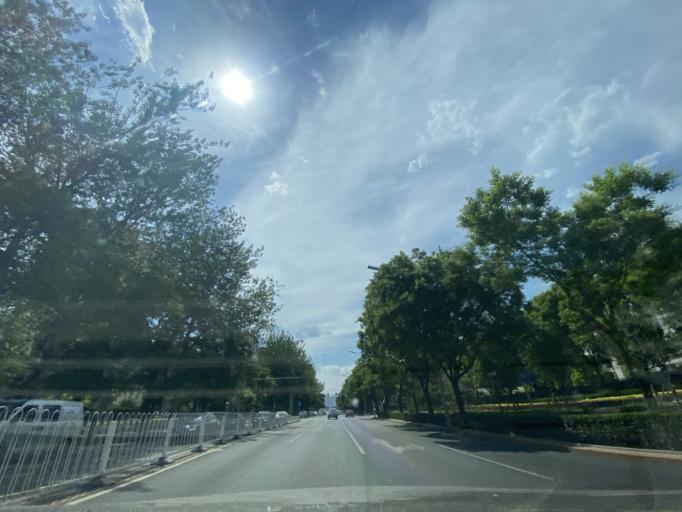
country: CN
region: Beijing
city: Lugu
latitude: 39.9062
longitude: 116.1893
